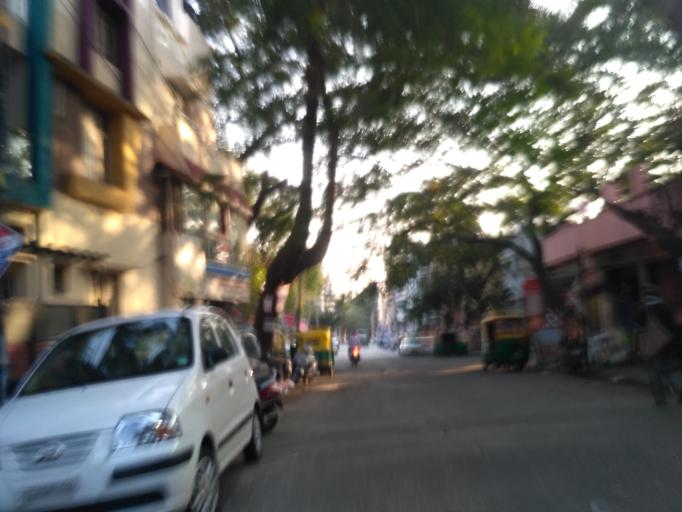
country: IN
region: Karnataka
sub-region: Bangalore Urban
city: Bangalore
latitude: 12.9654
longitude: 77.5383
